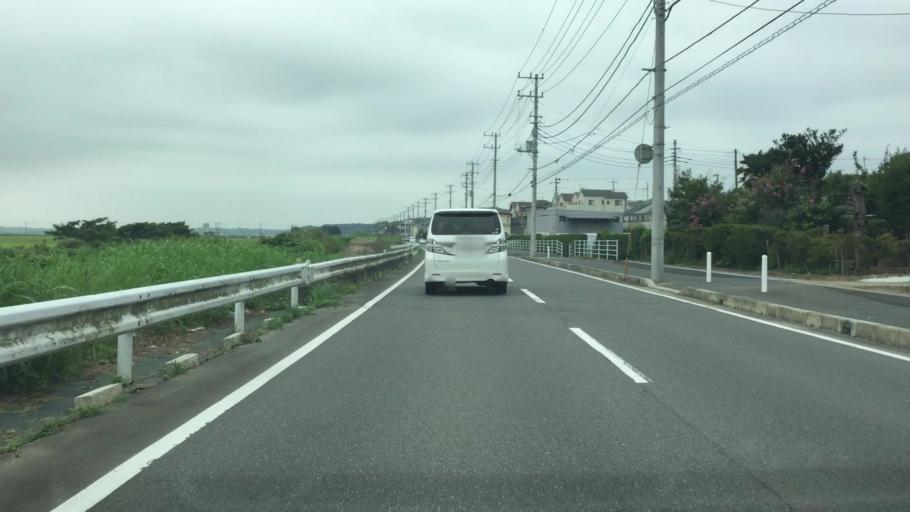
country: JP
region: Ibaraki
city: Toride
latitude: 35.8574
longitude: 140.1126
